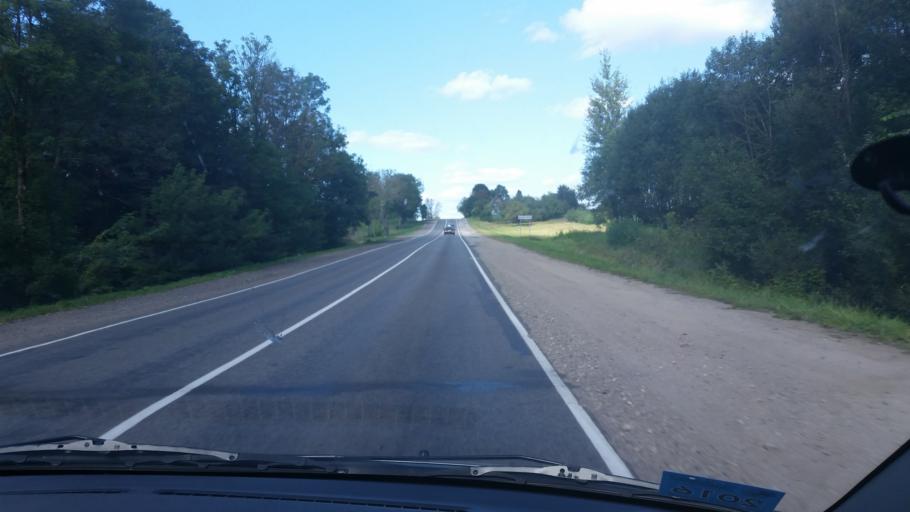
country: BY
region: Vitebsk
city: Vitebsk
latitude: 55.1085
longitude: 30.2834
